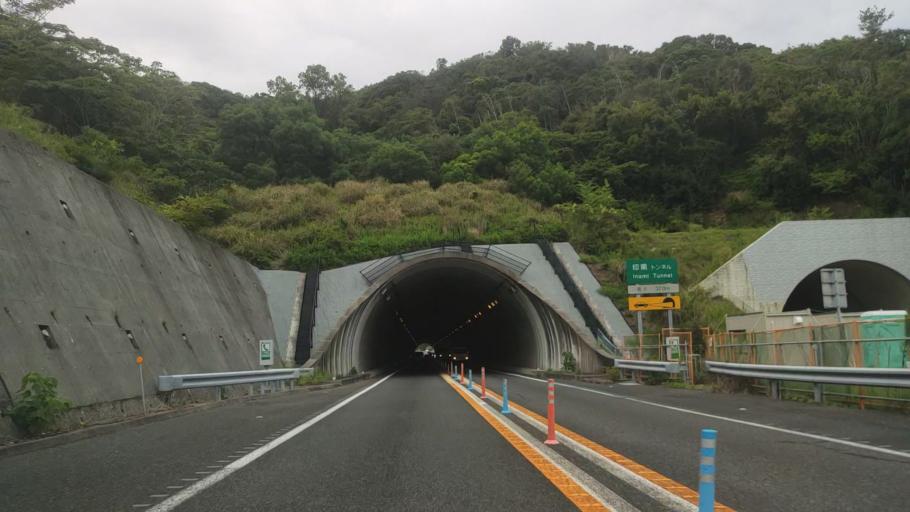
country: JP
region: Wakayama
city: Gobo
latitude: 33.8175
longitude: 135.2271
